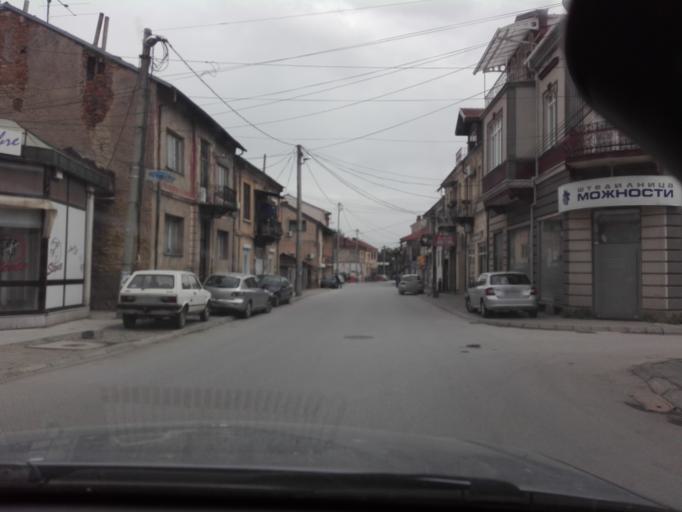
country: MK
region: Bitola
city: Bitola
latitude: 41.0281
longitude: 21.3383
